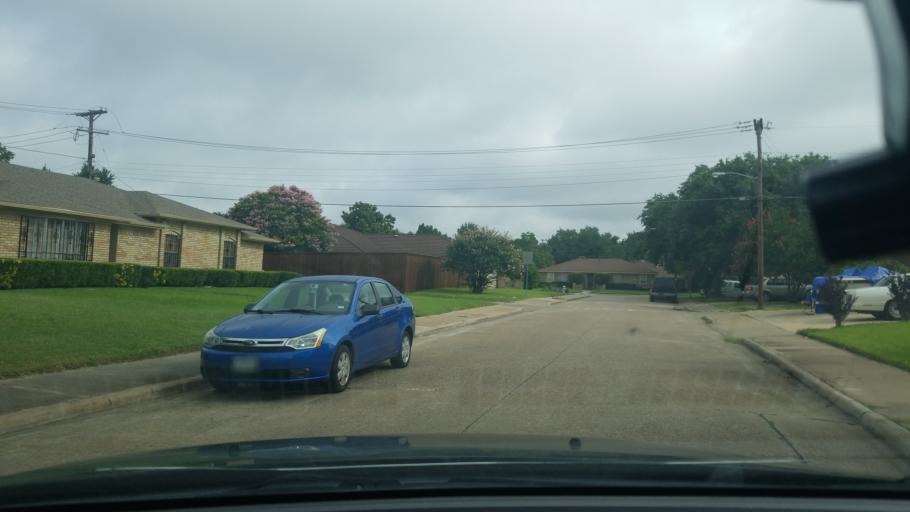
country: US
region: Texas
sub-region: Dallas County
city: Balch Springs
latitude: 32.7903
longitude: -96.6903
